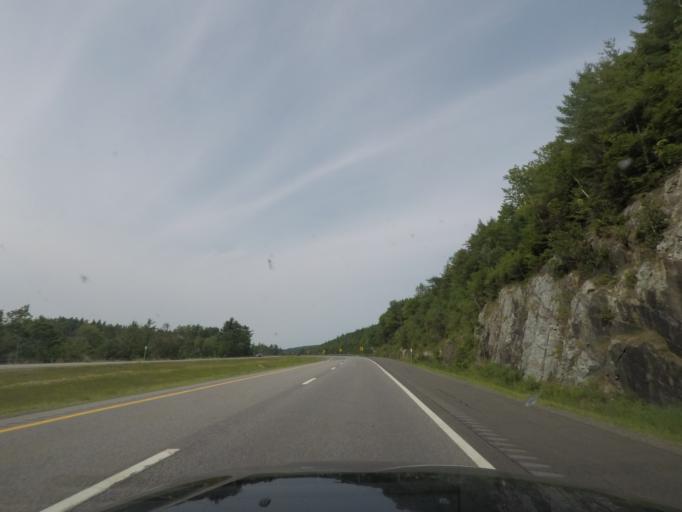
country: US
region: New York
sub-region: Essex County
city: Keeseville
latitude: 44.4089
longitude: -73.4974
